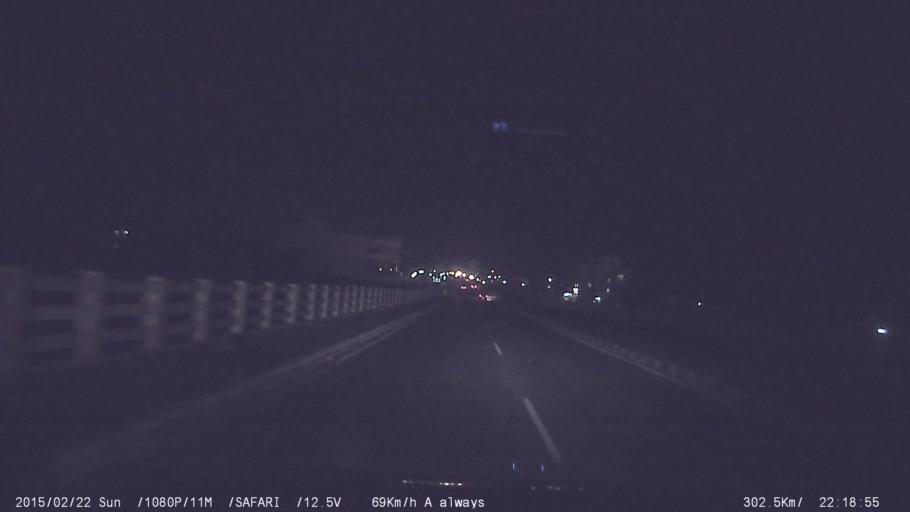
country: IN
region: Tamil Nadu
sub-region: Karur
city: Karur
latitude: 10.9741
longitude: 78.0630
